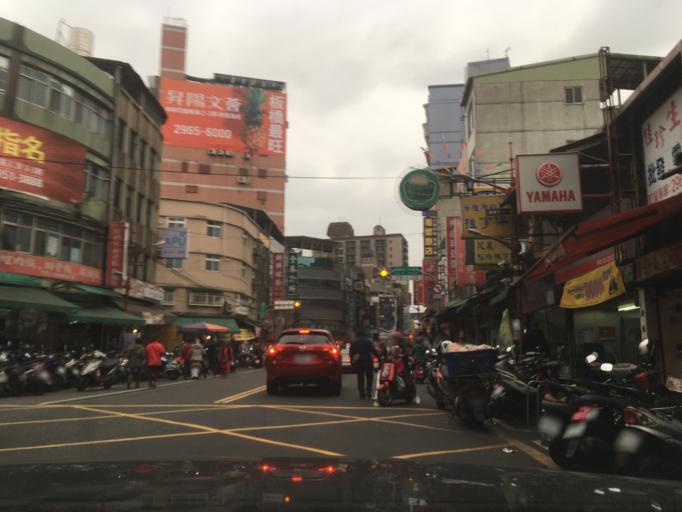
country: TW
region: Taipei
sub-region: Taipei
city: Banqiao
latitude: 25.0083
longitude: 121.4556
